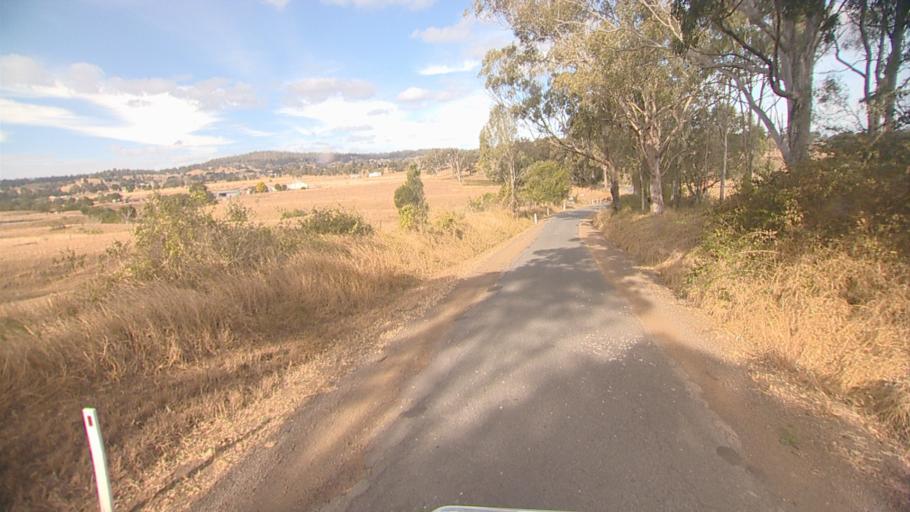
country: AU
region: Queensland
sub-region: Logan
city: Cedar Vale
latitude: -27.9165
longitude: 152.9996
